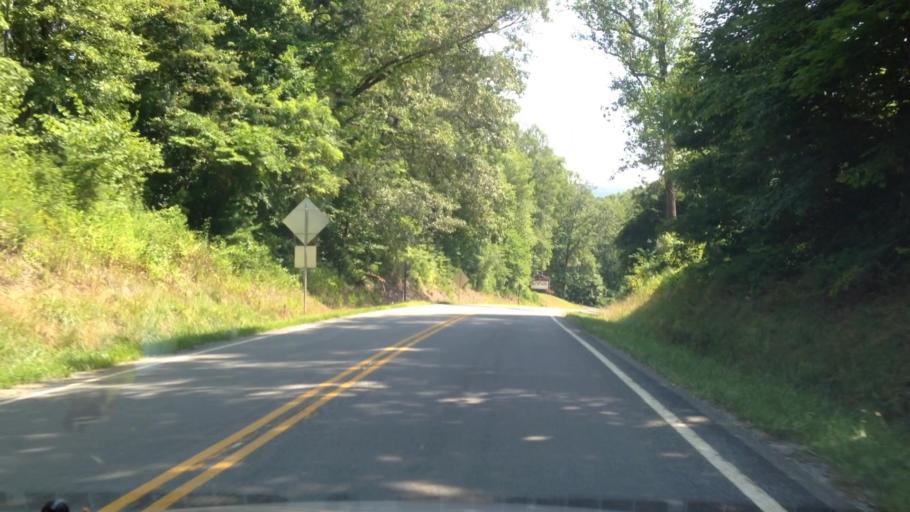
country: US
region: Virginia
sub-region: Patrick County
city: Stuart
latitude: 36.5928
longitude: -80.3164
